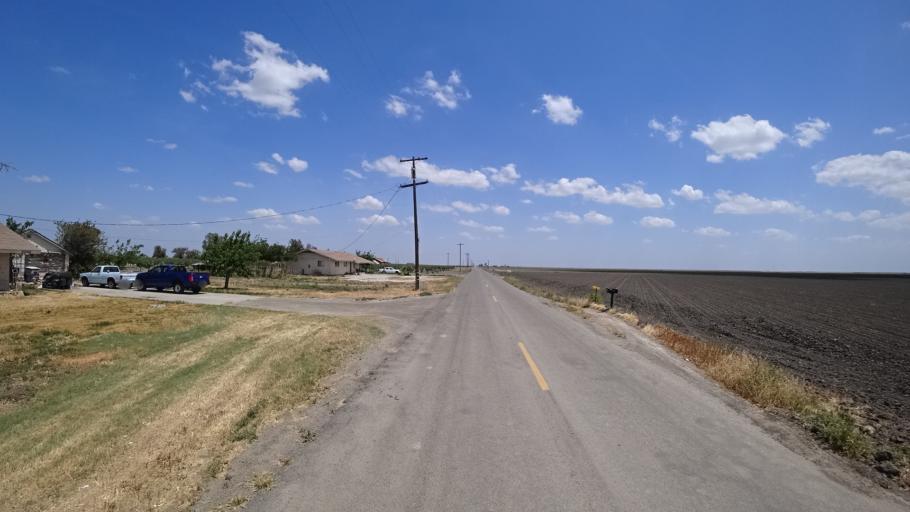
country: US
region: California
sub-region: Kings County
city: Stratford
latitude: 36.1527
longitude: -119.8184
